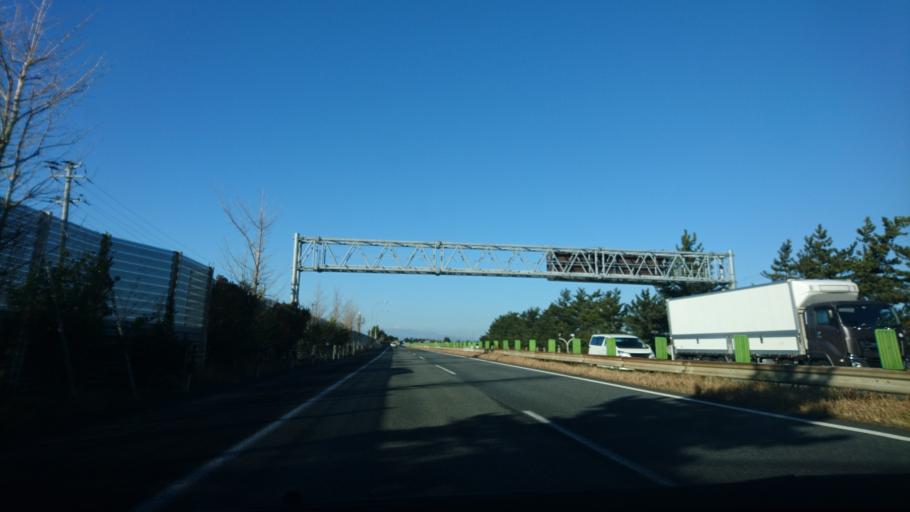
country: JP
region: Miyagi
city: Furukawa
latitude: 38.5590
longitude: 140.9300
